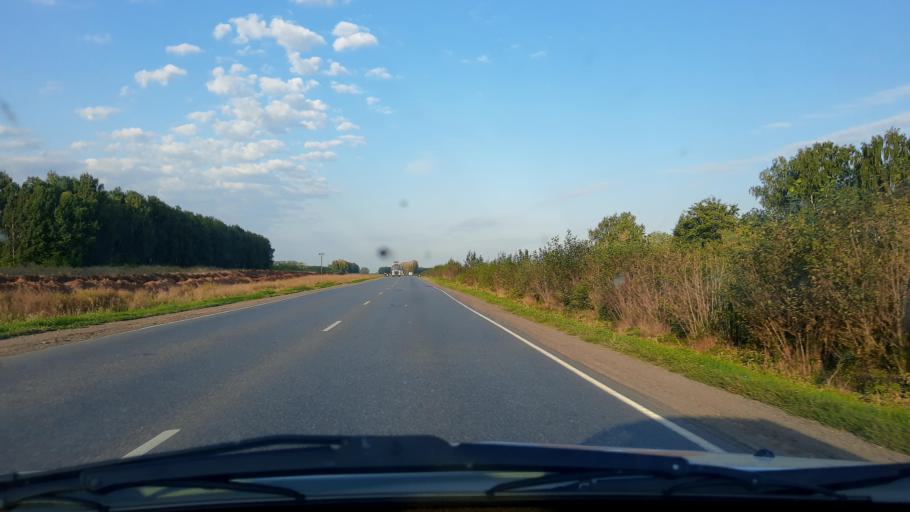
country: RU
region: Bashkortostan
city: Buzdyak
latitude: 54.6243
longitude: 54.4231
